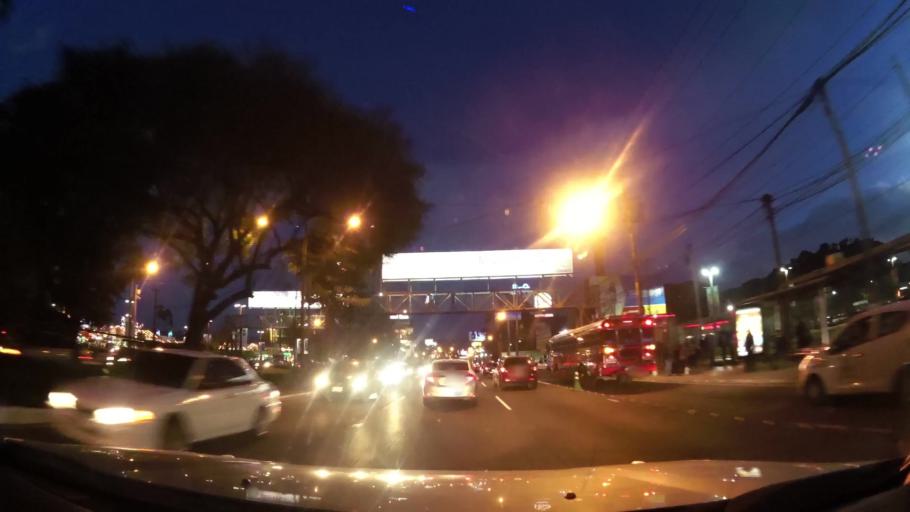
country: GT
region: Guatemala
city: Guatemala City
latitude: 14.6259
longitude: -90.5573
